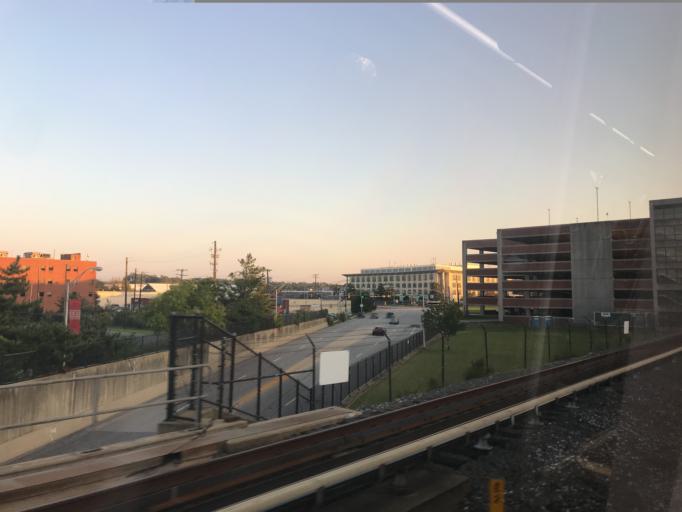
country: US
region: Maryland
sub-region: Prince George's County
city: College Park
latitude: 38.9807
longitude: -76.9275
